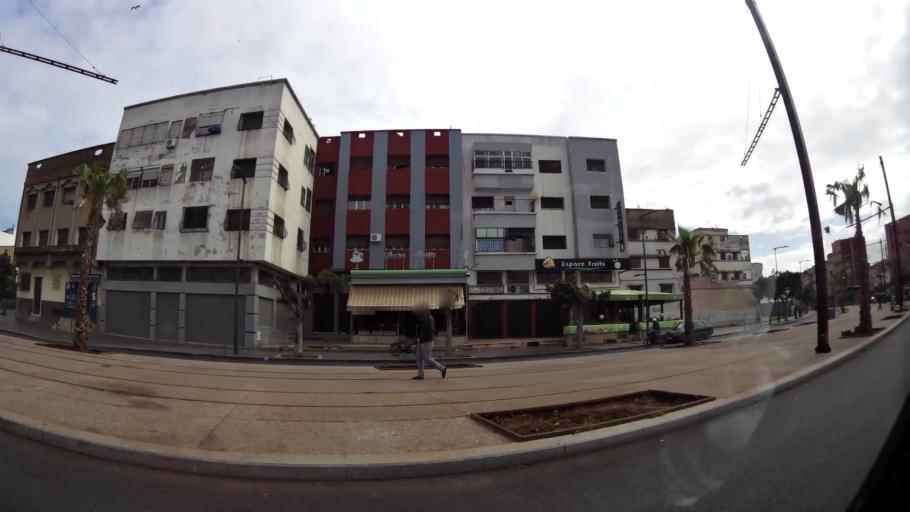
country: MA
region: Grand Casablanca
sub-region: Casablanca
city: Casablanca
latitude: 33.5717
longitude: -7.5887
